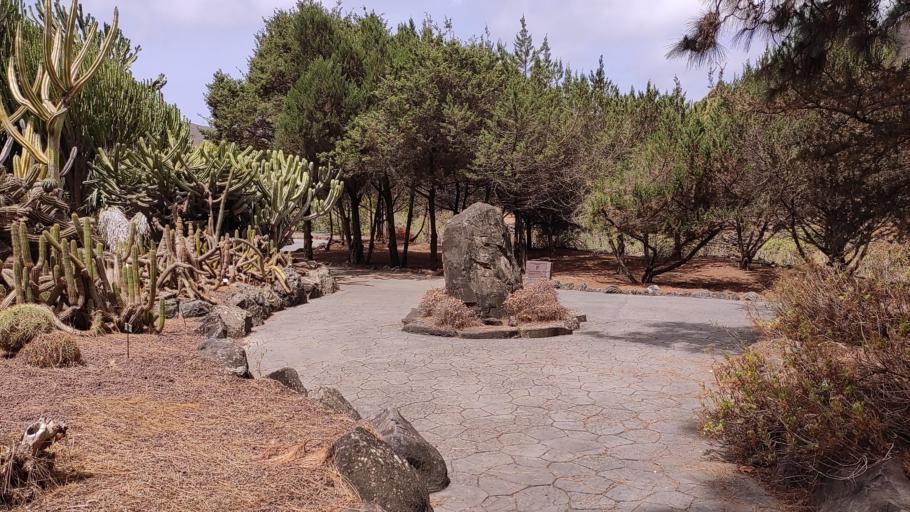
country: ES
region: Canary Islands
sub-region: Provincia de Las Palmas
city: Santa Brigida
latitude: 28.0637
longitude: -15.4621
